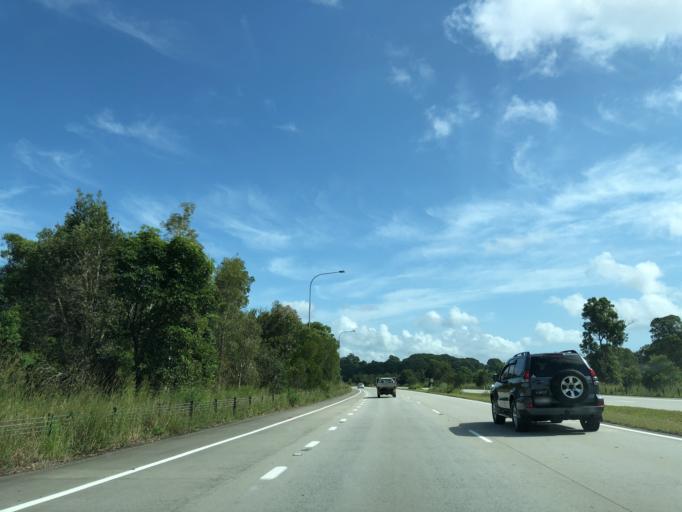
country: AU
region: New South Wales
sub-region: Byron Shire
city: Brunswick Heads
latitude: -28.5806
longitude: 153.5443
